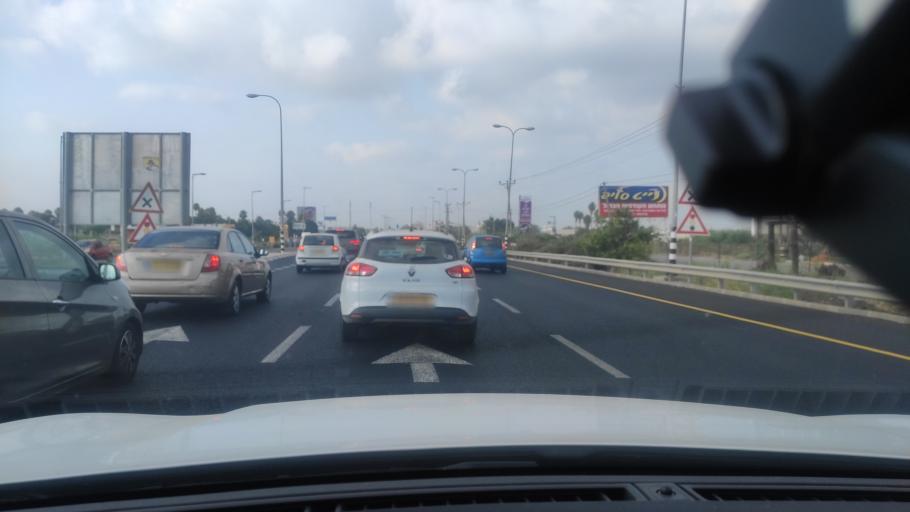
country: IL
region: Central District
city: Petah Tiqwa
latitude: 32.1180
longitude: 34.9031
